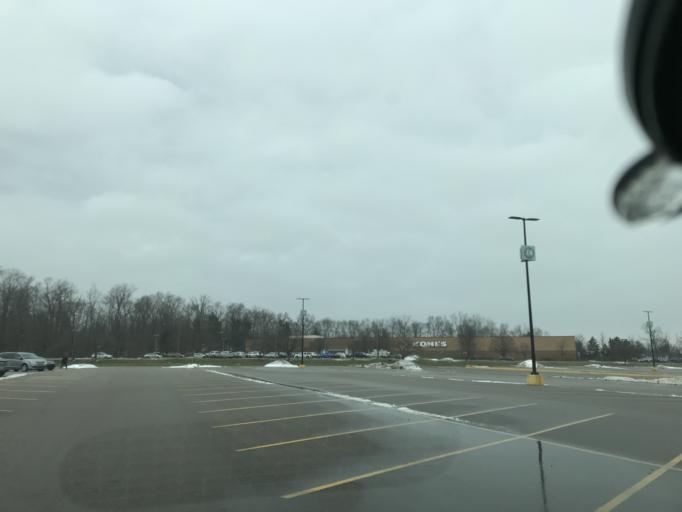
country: US
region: Michigan
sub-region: Kent County
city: East Grand Rapids
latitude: 42.9169
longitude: -85.5906
